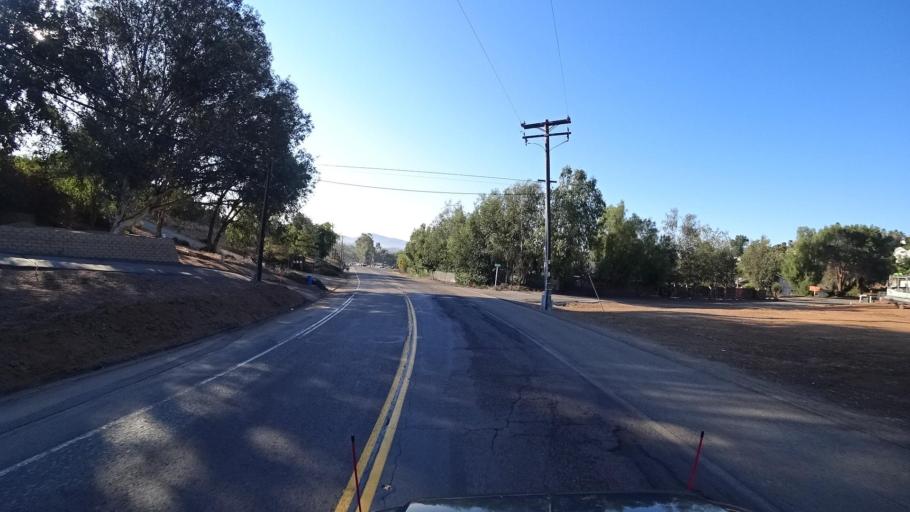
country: US
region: California
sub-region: San Diego County
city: Escondido
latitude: 33.1182
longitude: -117.0609
